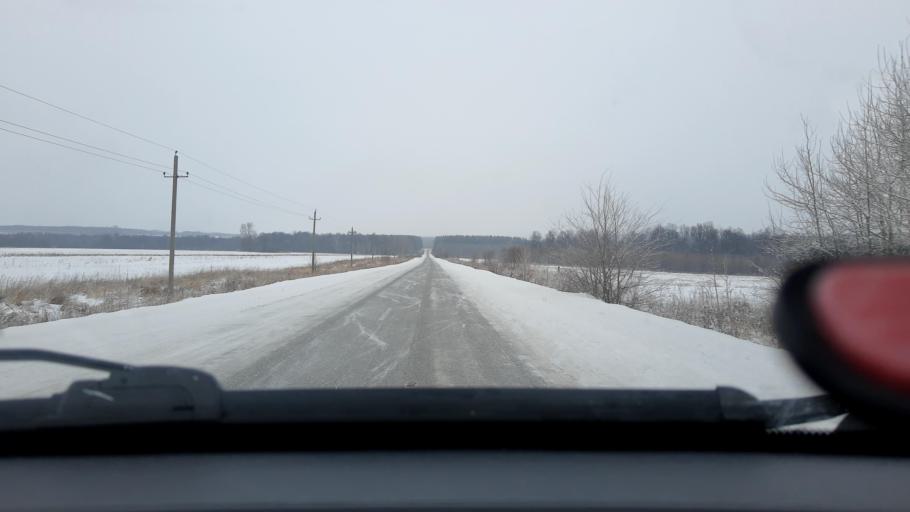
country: RU
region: Bashkortostan
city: Iglino
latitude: 54.6646
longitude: 56.4228
